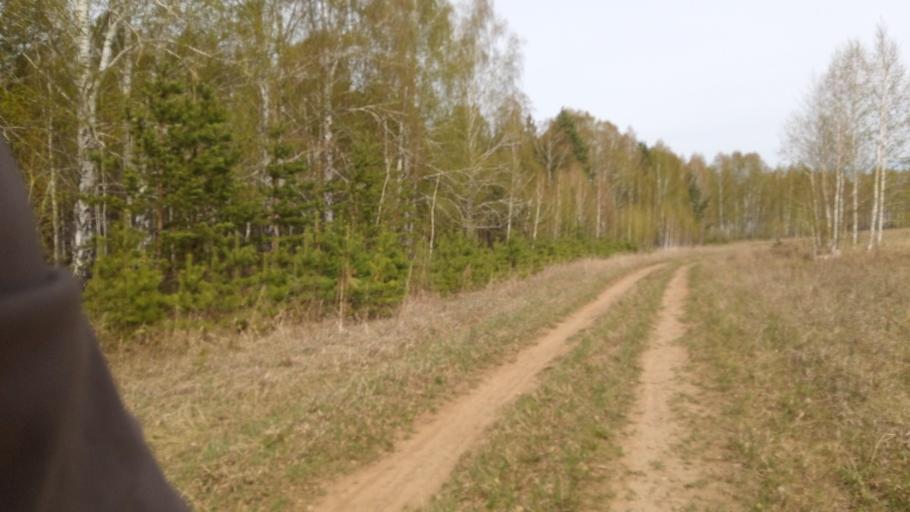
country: RU
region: Chelyabinsk
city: Timiryazevskiy
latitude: 55.0207
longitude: 60.8592
